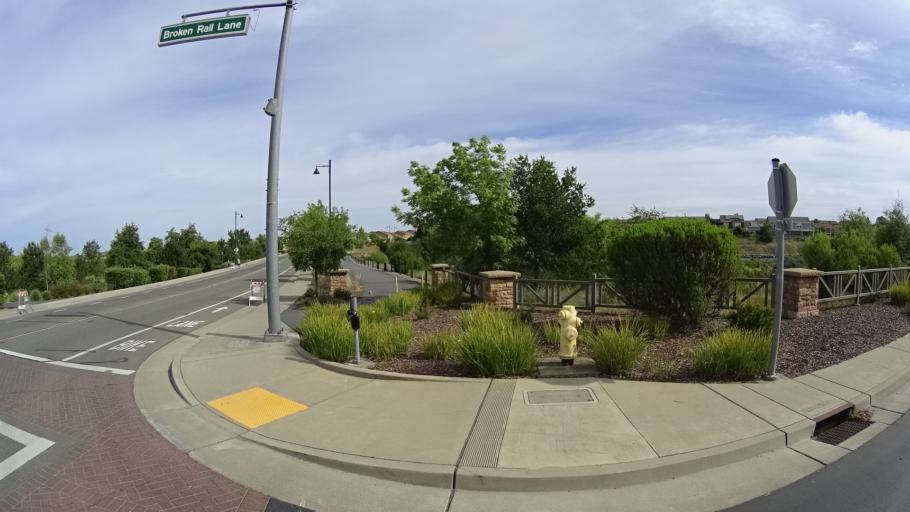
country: US
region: California
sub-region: Placer County
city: Lincoln
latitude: 38.8329
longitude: -121.2800
